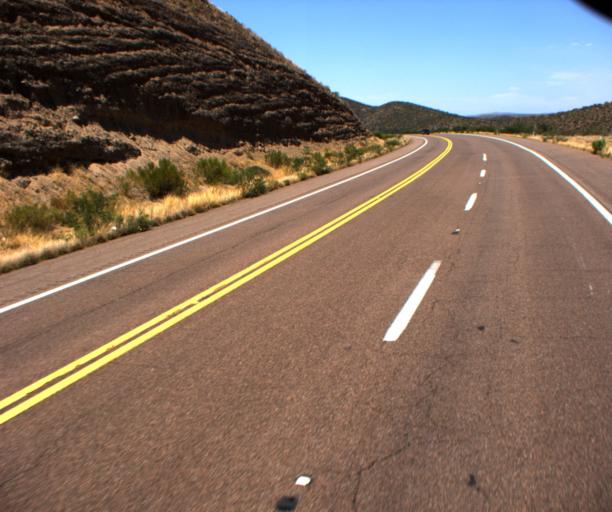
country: US
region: Arizona
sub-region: Gila County
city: Tonto Basin
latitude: 33.9862
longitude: -111.3120
